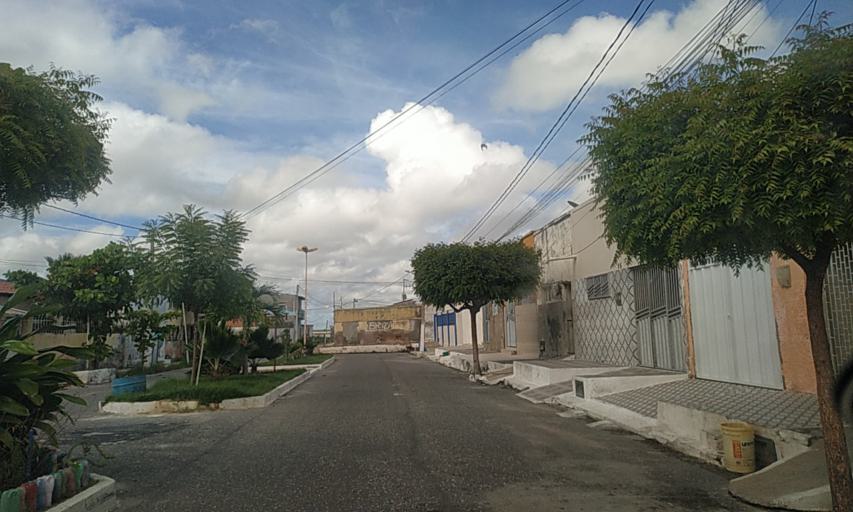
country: BR
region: Rio Grande do Norte
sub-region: Areia Branca
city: Areia Branca
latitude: -4.9573
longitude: -37.1314
